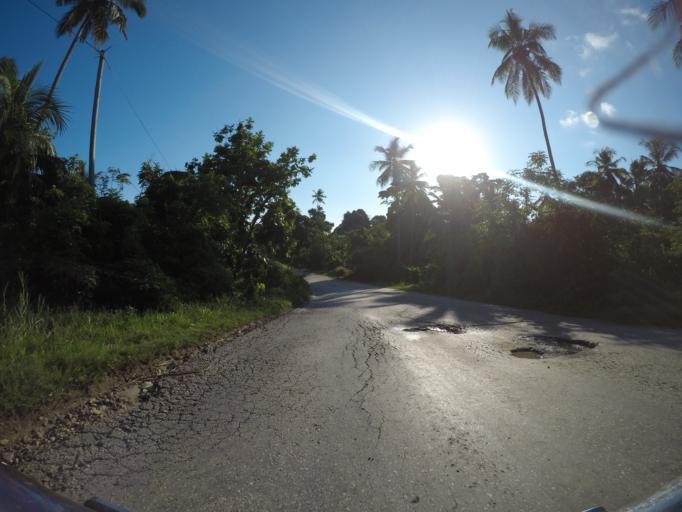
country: TZ
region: Pemba South
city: Mtambile
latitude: -5.3699
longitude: 39.7081
